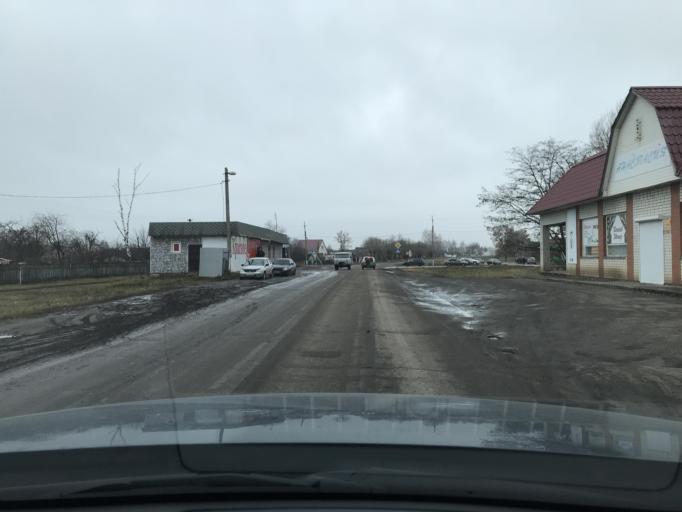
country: RU
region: Penza
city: Zemetchino
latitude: 53.5013
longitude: 42.6308
